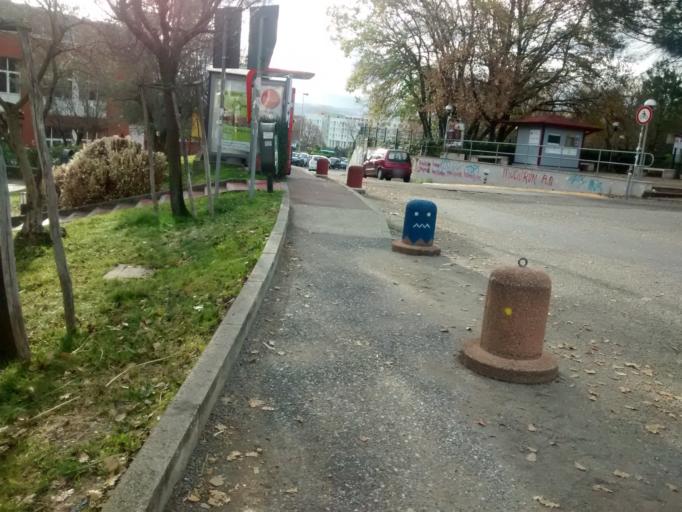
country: IT
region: Calabria
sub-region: Provincia di Cosenza
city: Quattromiglia
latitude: 39.3568
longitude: 16.2258
